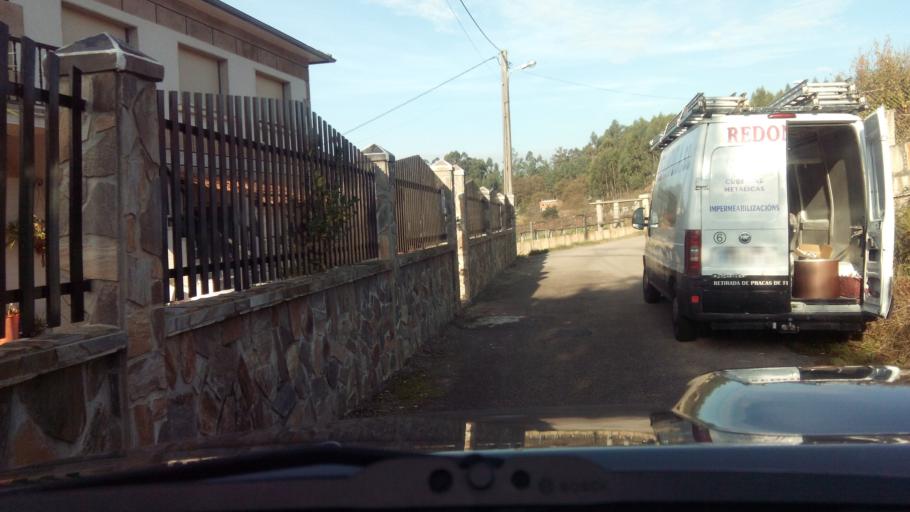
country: ES
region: Galicia
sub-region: Provincia de Pontevedra
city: Marin
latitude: 42.3616
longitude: -8.7096
